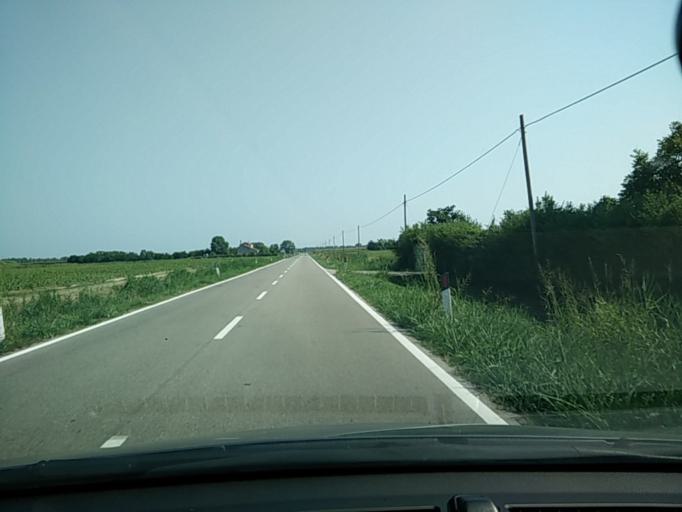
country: IT
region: Veneto
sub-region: Provincia di Venezia
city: La Salute di Livenza
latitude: 45.6341
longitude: 12.8327
